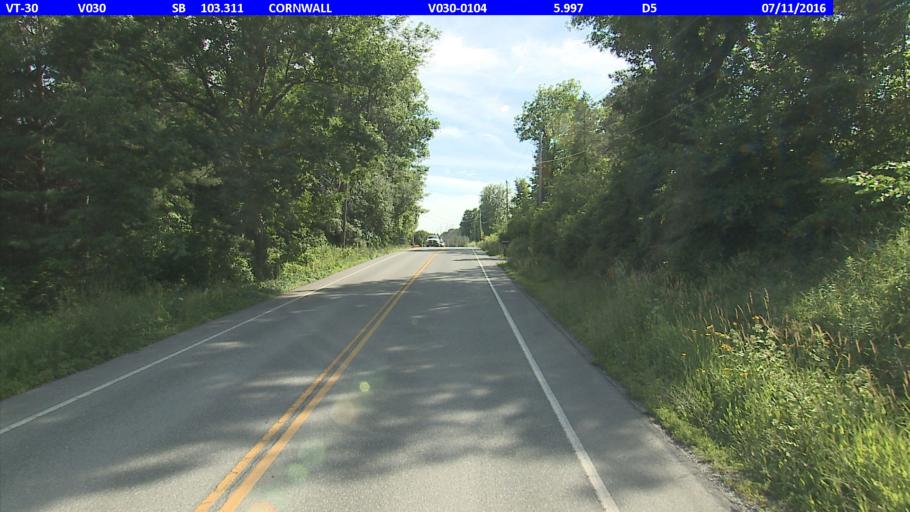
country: US
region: Vermont
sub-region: Addison County
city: Middlebury (village)
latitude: 43.9911
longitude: -73.1944
